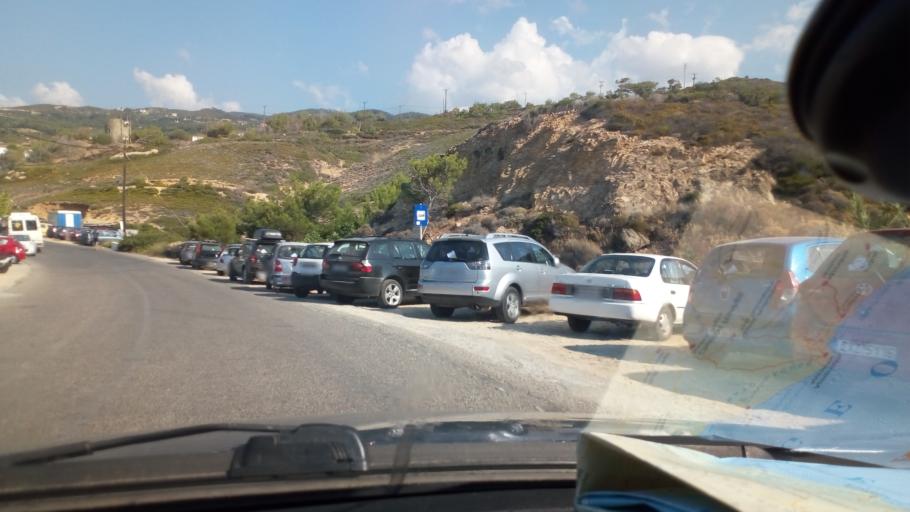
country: GR
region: North Aegean
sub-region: Nomos Samou
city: Agios Kirykos
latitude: 37.6302
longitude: 26.0943
